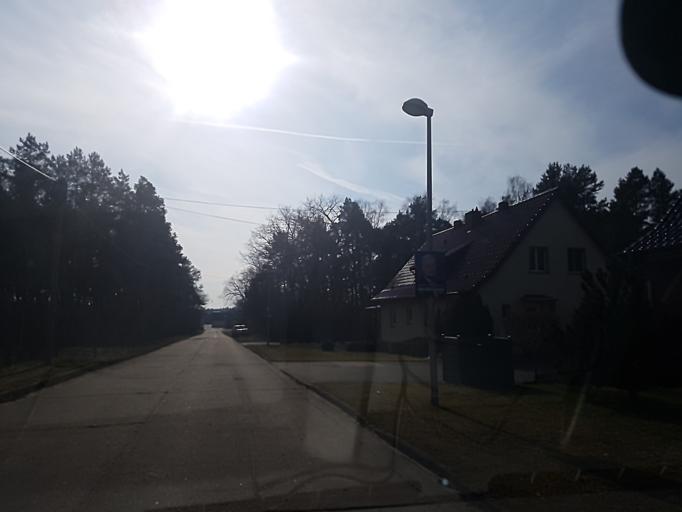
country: DE
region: Brandenburg
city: Wenzlow
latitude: 52.3289
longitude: 12.4401
